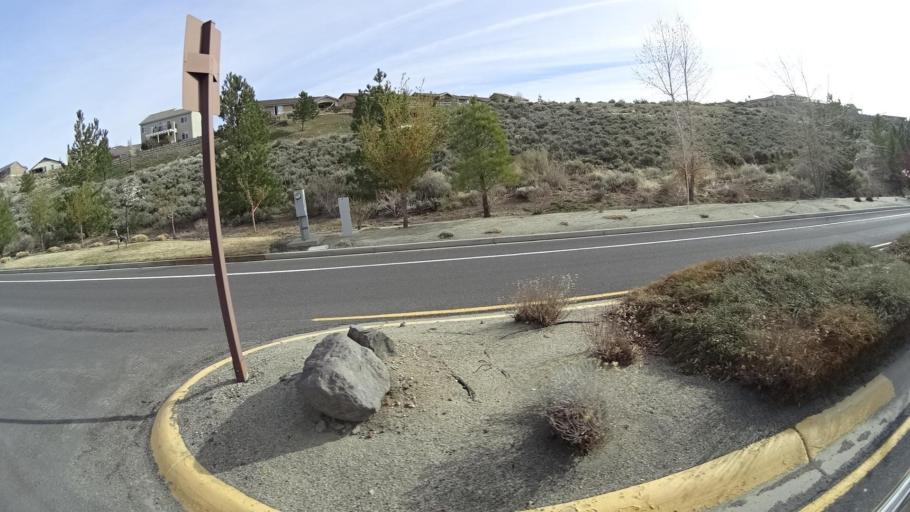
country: US
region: Nevada
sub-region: Washoe County
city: Mogul
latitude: 39.5261
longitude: -119.9475
